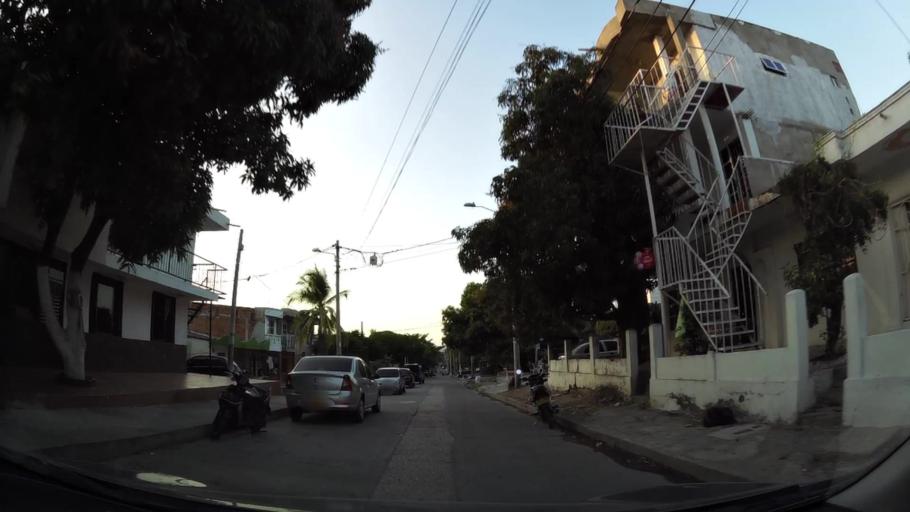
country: CO
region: Bolivar
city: Cartagena
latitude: 10.3859
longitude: -75.4916
